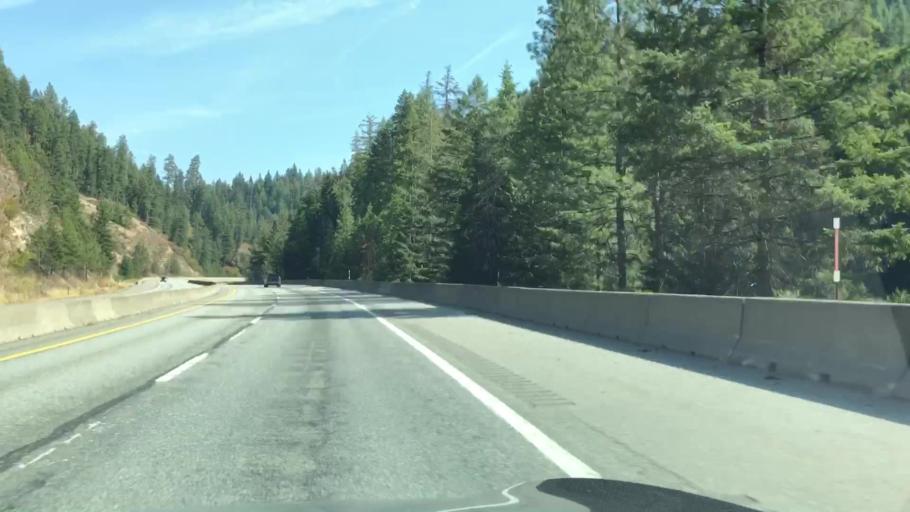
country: US
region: Idaho
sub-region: Kootenai County
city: Coeur d'Alene
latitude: 47.6277
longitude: -116.5941
